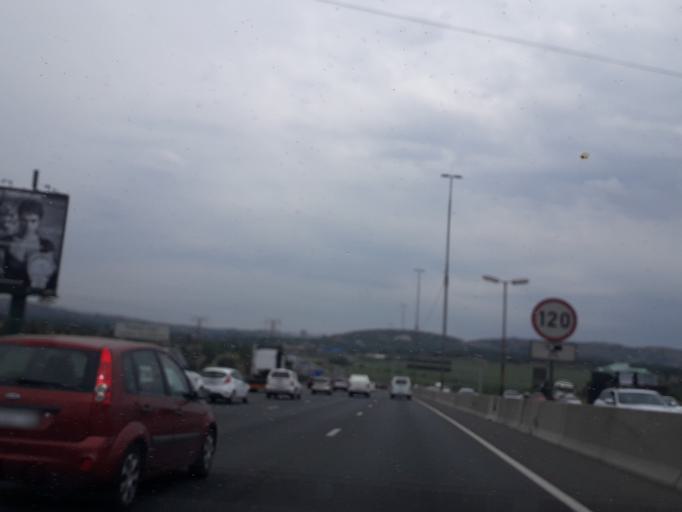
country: ZA
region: Gauteng
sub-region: City of Johannesburg Metropolitan Municipality
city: Modderfontein
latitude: -26.1310
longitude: 28.1341
